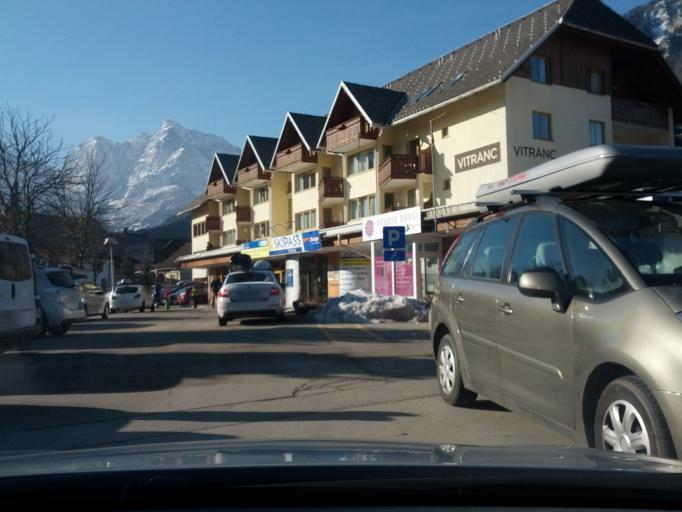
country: SI
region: Kranjska Gora
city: Kranjska Gora
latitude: 46.4841
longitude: 13.7821
